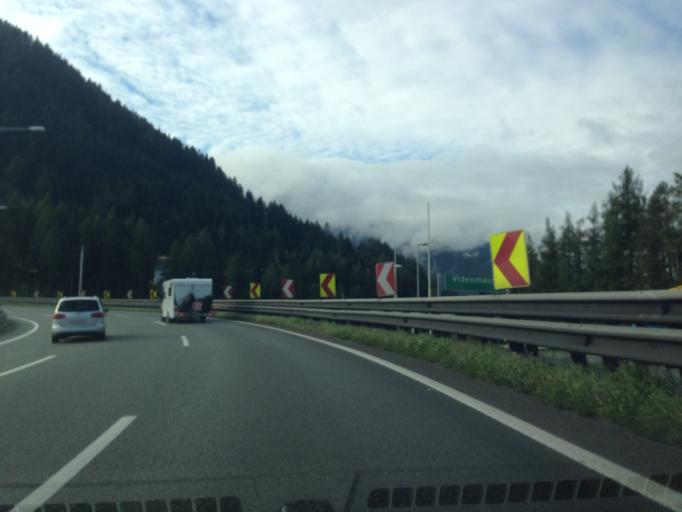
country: AT
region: Tyrol
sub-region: Politischer Bezirk Innsbruck Land
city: Schoenberg im Stubaital
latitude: 47.1834
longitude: 11.3971
